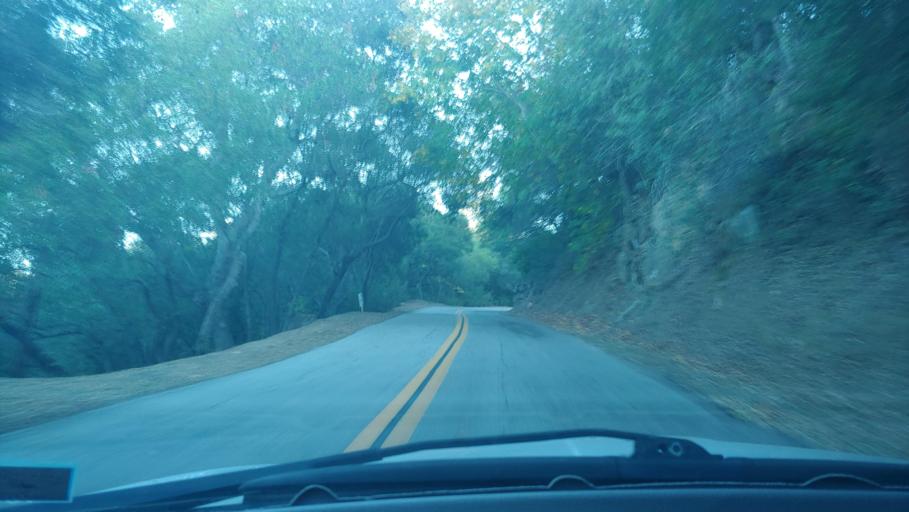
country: US
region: California
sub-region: Santa Barbara County
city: Goleta
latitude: 34.5146
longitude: -119.8289
